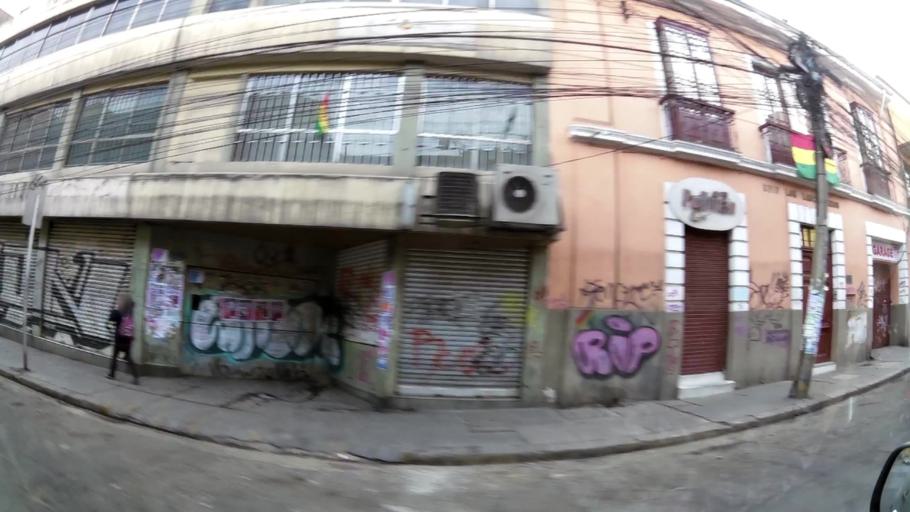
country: BO
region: La Paz
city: La Paz
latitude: -16.5013
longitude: -68.1341
